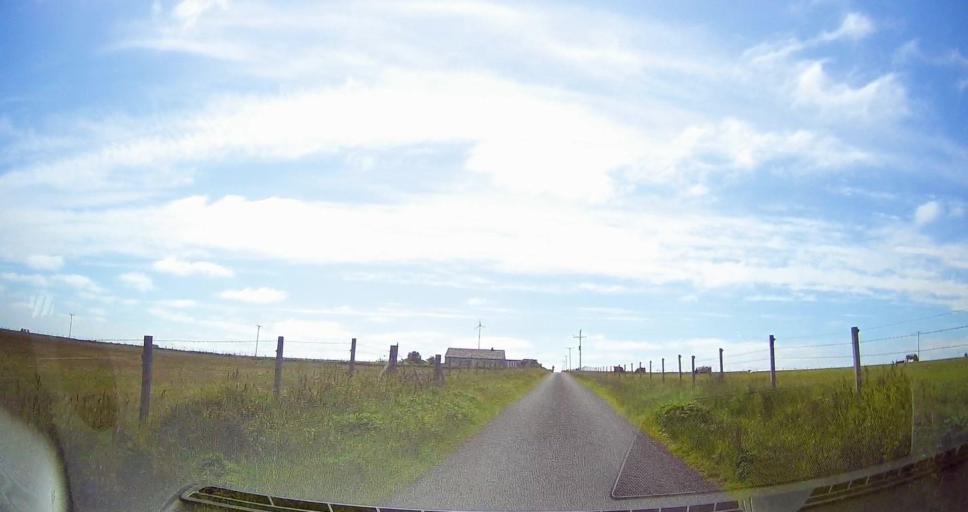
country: GB
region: Scotland
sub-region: Orkney Islands
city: Kirkwall
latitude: 58.8330
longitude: -2.8996
